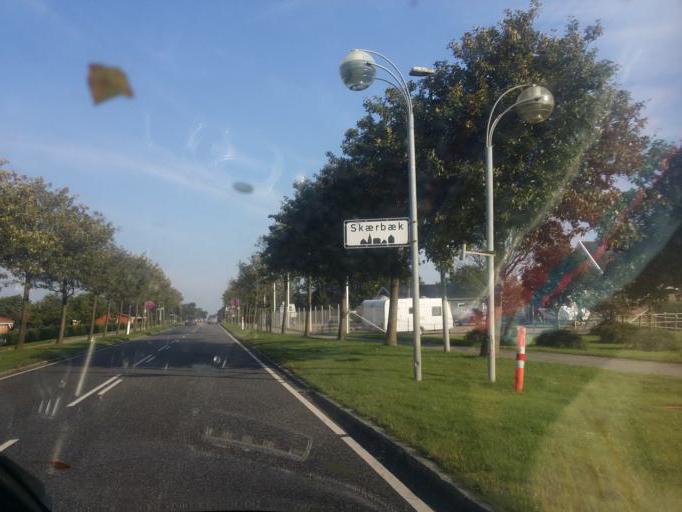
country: DK
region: South Denmark
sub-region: Tonder Kommune
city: Sherrebek
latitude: 55.1507
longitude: 8.7789
